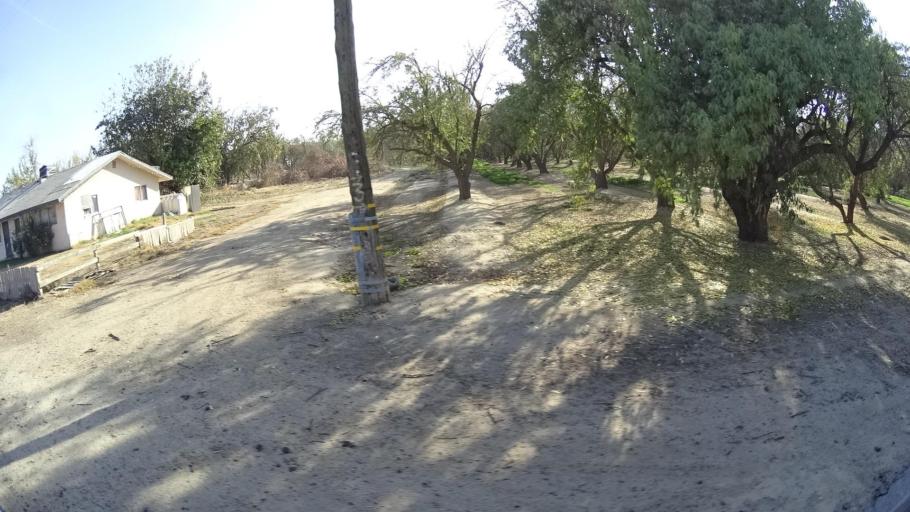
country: US
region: California
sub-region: Kern County
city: McFarland
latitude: 35.7033
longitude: -119.2550
